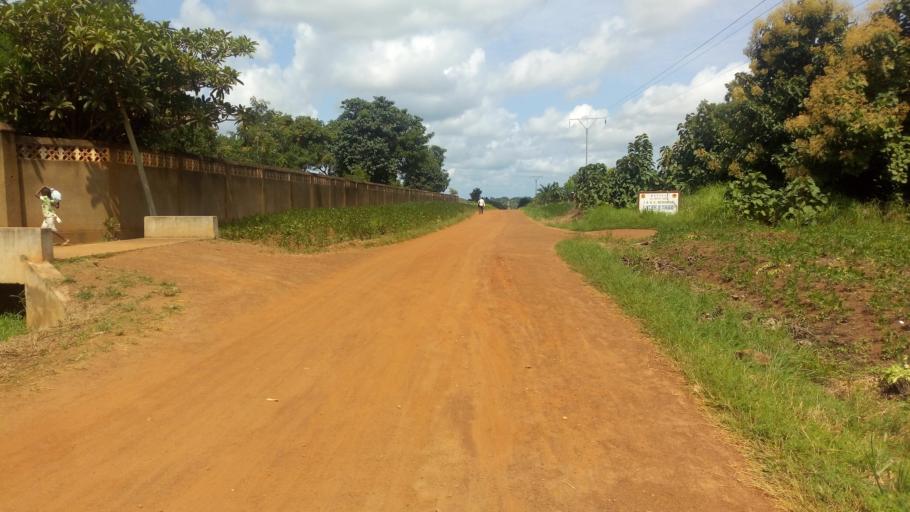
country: TG
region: Centrale
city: Sotouboua
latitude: 8.4330
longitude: 1.0010
